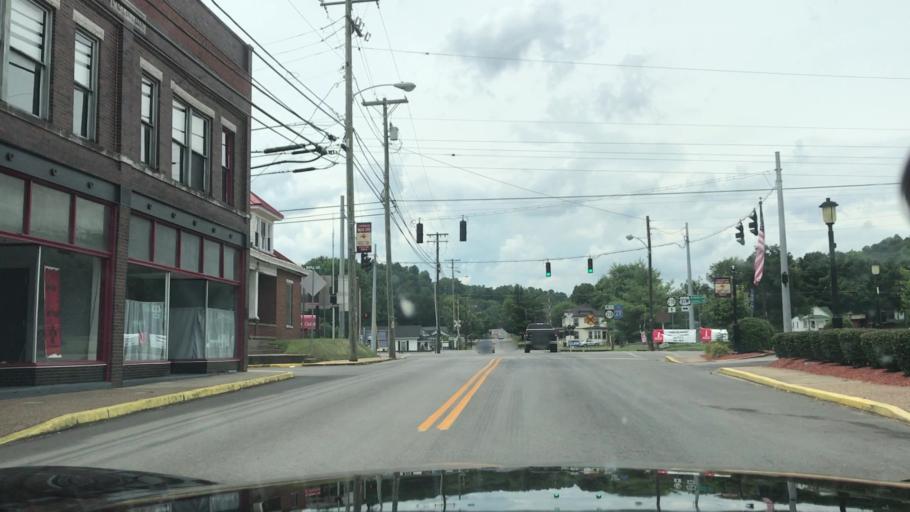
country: US
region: Kentucky
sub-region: Hart County
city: Horse Cave
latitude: 37.1795
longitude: -85.9067
